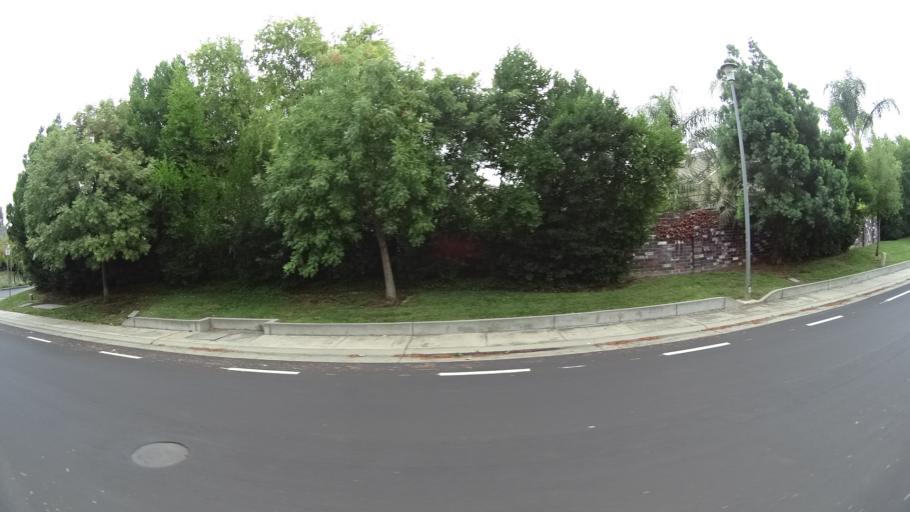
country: US
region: California
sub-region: Sacramento County
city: Laguna
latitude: 38.4099
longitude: -121.4305
